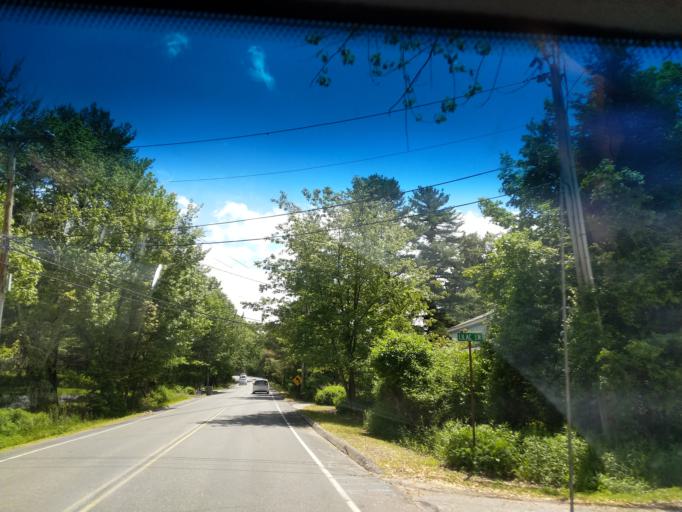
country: US
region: Maine
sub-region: Cumberland County
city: Falmouth
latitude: 43.7281
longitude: -70.2756
